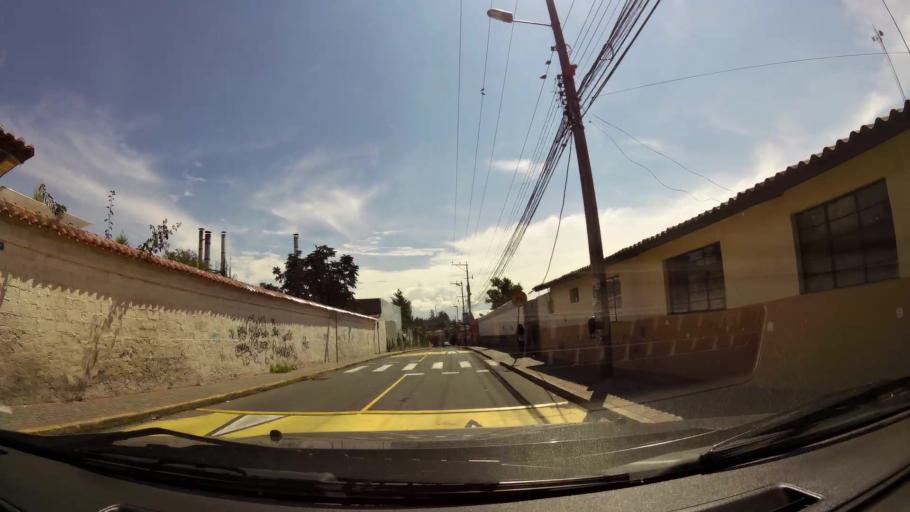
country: EC
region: Pichincha
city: Quito
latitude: -0.2006
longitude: -78.4287
